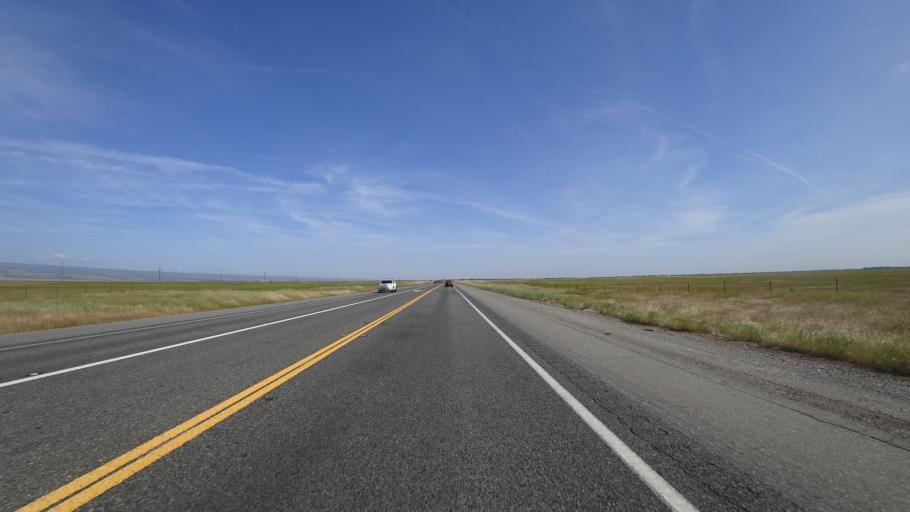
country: US
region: California
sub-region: Tehama County
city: Los Molinos
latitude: 39.9130
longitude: -122.0115
